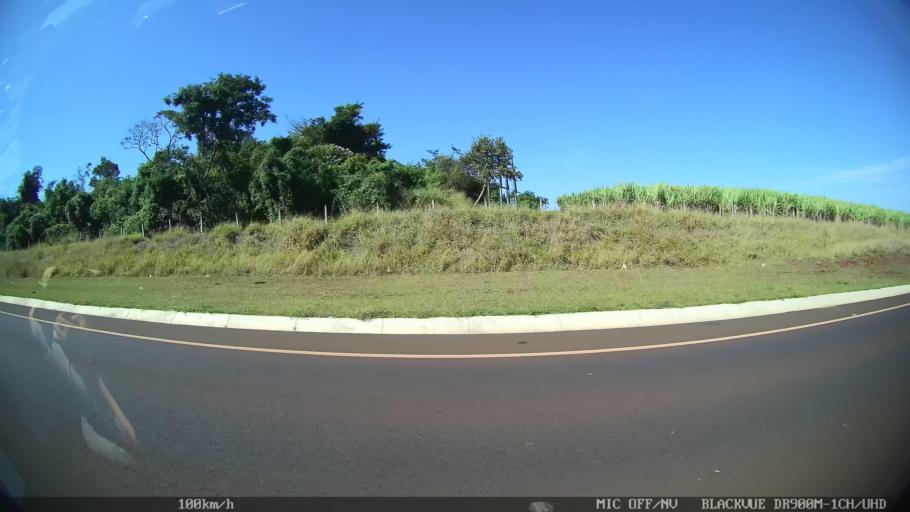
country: BR
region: Sao Paulo
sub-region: Franca
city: Franca
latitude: -20.6534
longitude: -47.4884
